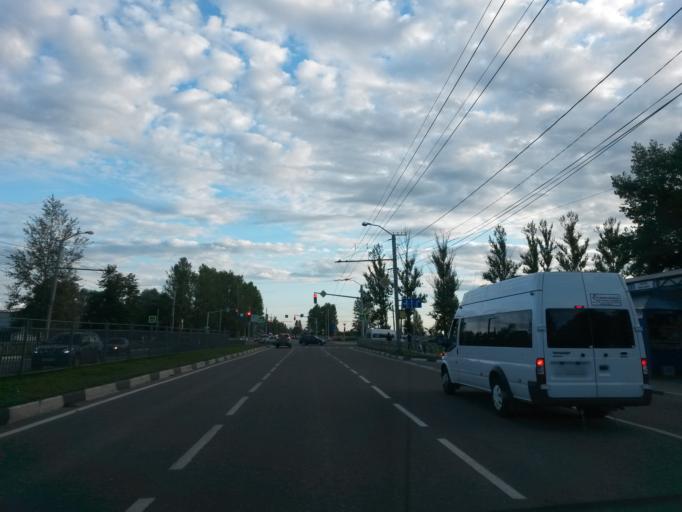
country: RU
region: Jaroslavl
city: Yaroslavl
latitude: 57.6755
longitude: 39.7744
